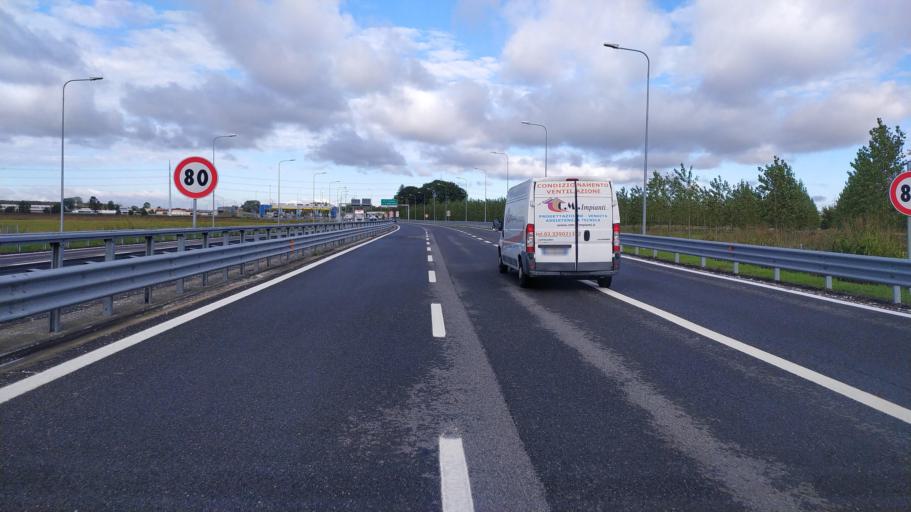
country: IT
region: Lombardy
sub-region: Provincia di Pavia
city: Trivolzio
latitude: 45.2454
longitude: 9.0532
